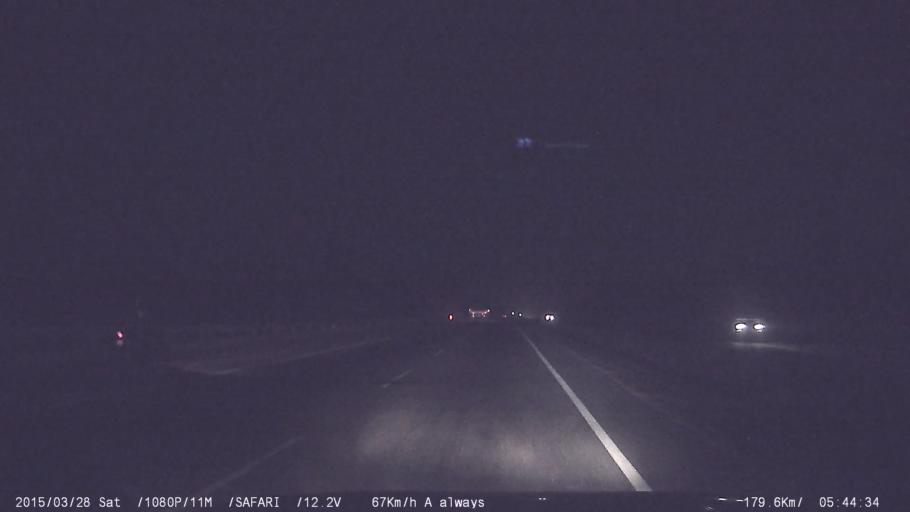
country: IN
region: Karnataka
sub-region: Bangalore Urban
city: Bangalore
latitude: 12.8535
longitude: 77.5413
